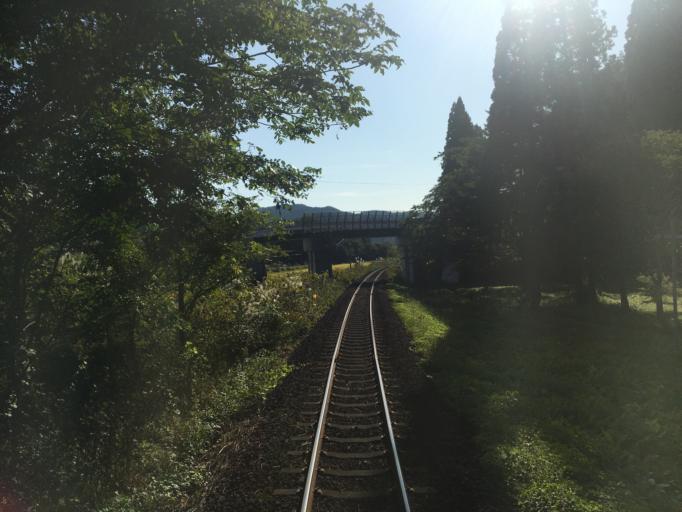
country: JP
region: Akita
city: Kakunodatemachi
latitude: 39.7500
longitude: 140.5971
